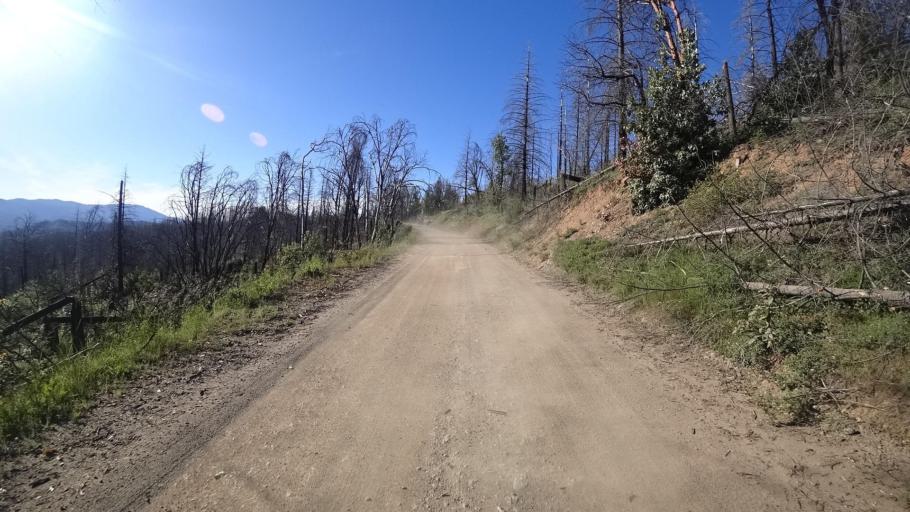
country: US
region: California
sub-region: Lake County
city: Upper Lake
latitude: 39.3397
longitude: -122.9585
